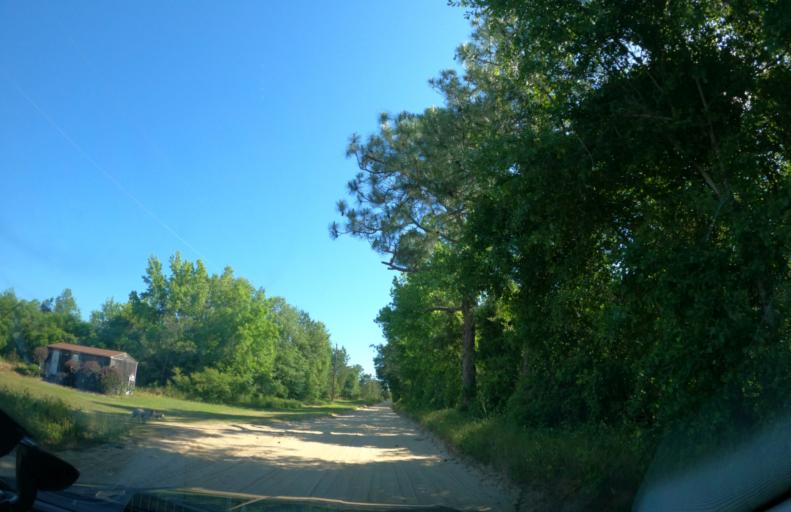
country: US
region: Georgia
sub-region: Jefferson County
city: Wrens
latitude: 33.2173
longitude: -82.3568
